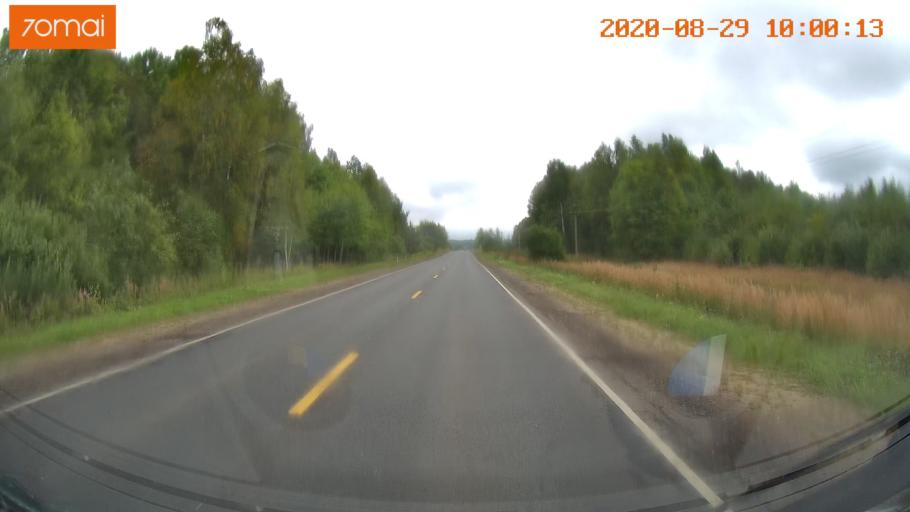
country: RU
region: Ivanovo
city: Zarechnyy
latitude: 57.4099
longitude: 42.3875
